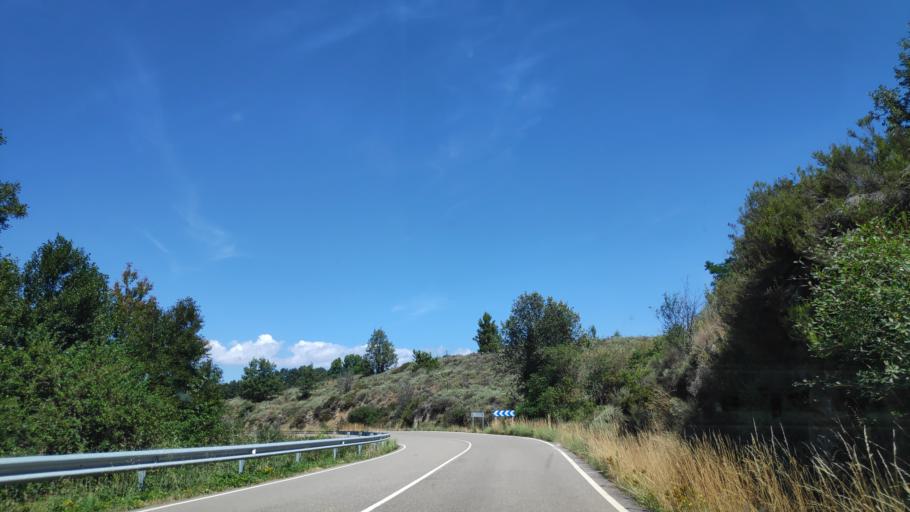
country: ES
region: Castille and Leon
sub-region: Provincia de Zamora
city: Puebla de Sanabria
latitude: 42.0572
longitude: -6.6432
